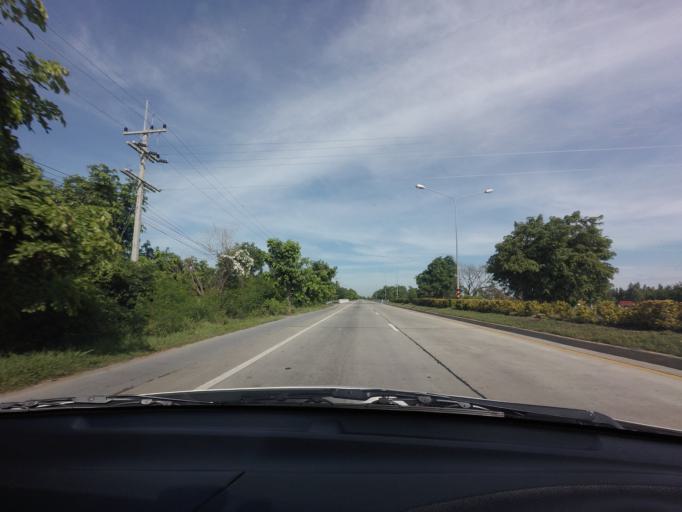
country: TH
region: Suphan Buri
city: Suphan Buri
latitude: 14.4557
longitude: 100.0647
